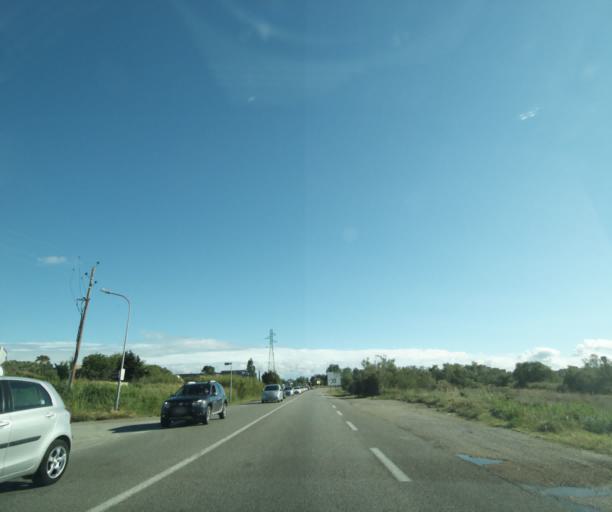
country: FR
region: Provence-Alpes-Cote d'Azur
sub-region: Departement des Bouches-du-Rhone
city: Vitrolles
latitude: 43.4506
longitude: 5.2309
